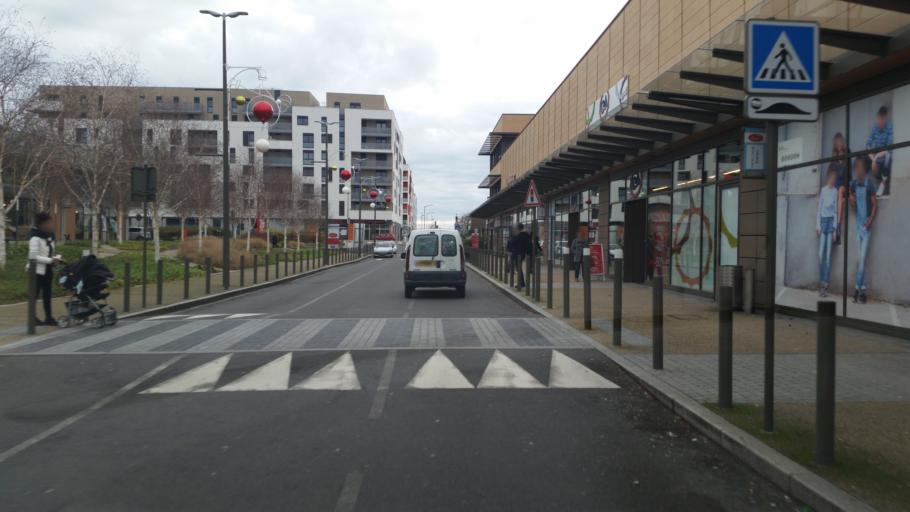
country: FR
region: Ile-de-France
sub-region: Departement du Val-de-Marne
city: Fresnes
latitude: 48.7541
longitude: 2.3284
